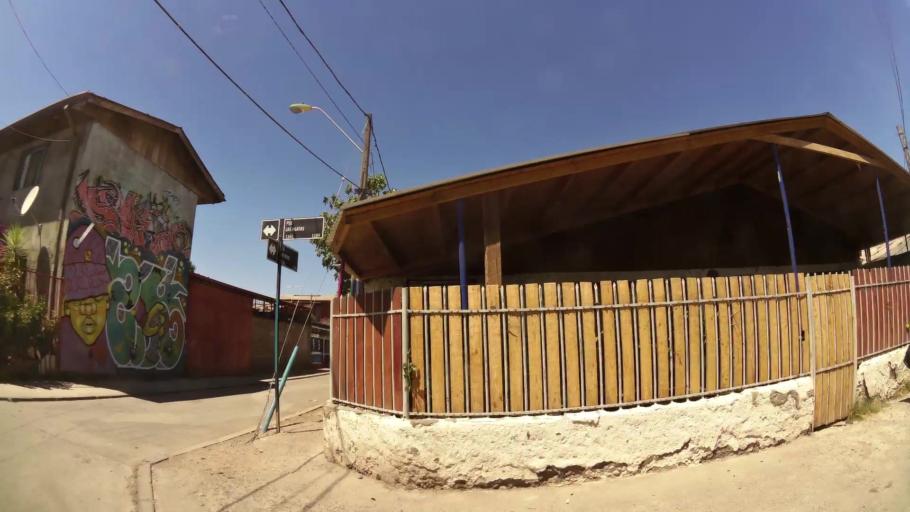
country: CL
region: Santiago Metropolitan
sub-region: Provincia de Santiago
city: La Pintana
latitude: -33.5664
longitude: -70.6638
